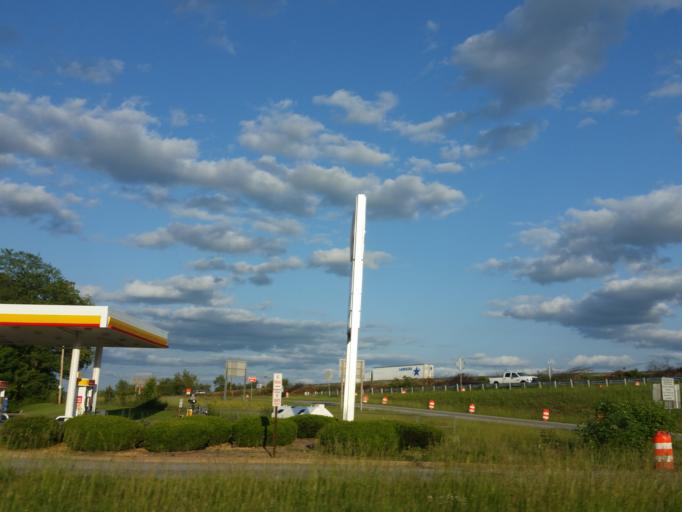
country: US
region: Virginia
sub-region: Washington County
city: Abingdon
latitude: 36.6947
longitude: -82.0117
